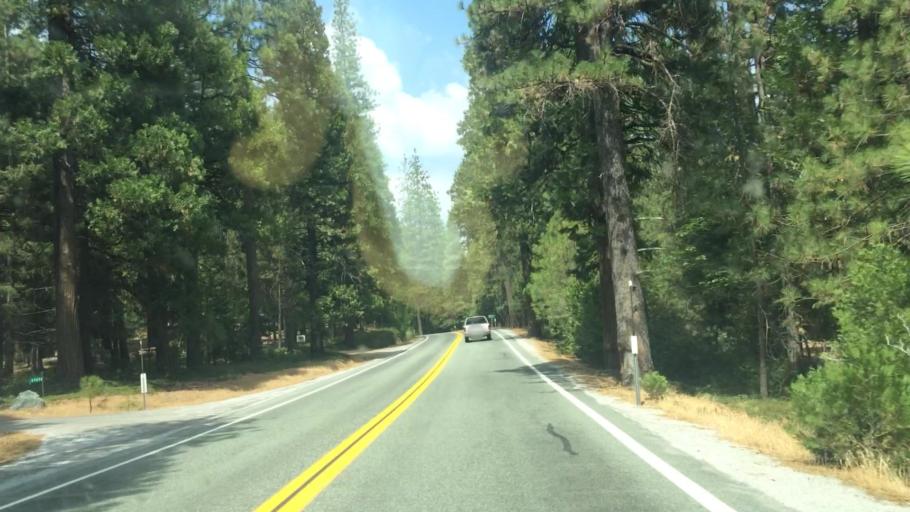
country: US
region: California
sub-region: Amador County
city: Pioneer
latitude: 38.4942
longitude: -120.5087
